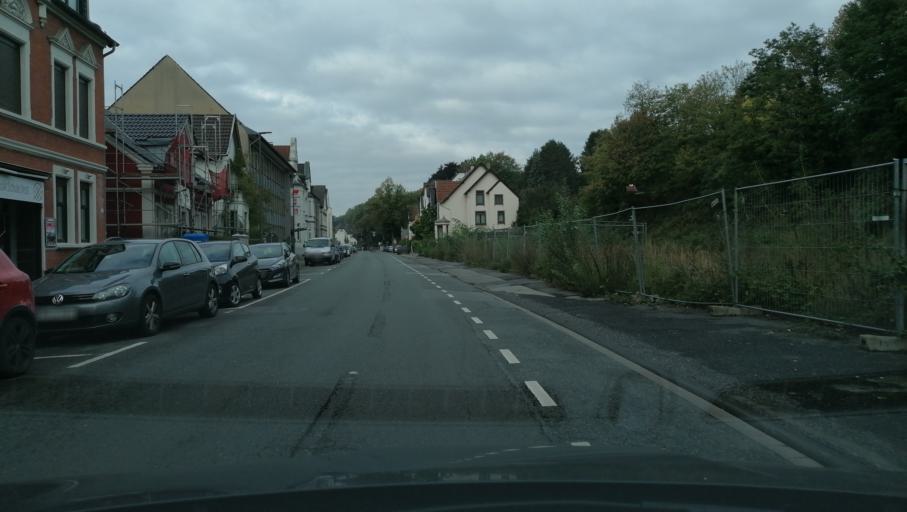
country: DE
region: North Rhine-Westphalia
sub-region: Regierungsbezirk Munster
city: Recklinghausen
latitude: 51.6183
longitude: 7.1927
